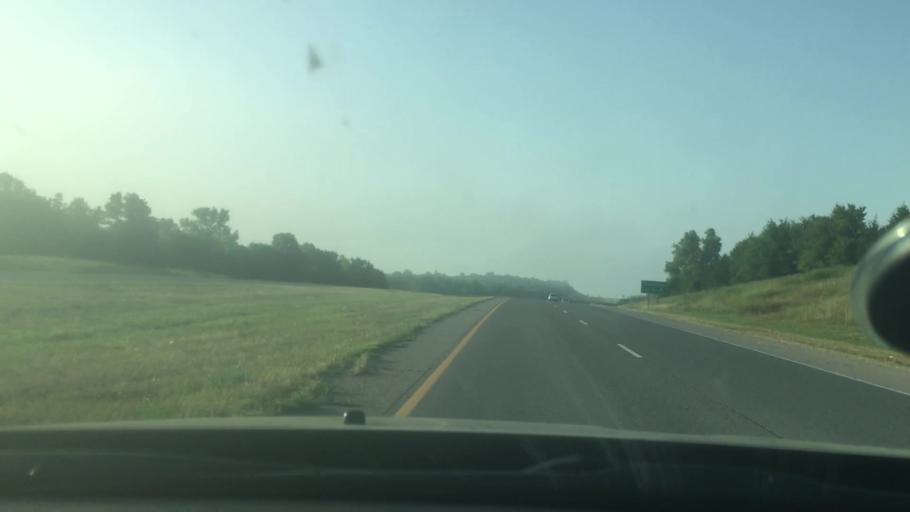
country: US
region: Oklahoma
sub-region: Pontotoc County
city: Ada
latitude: 34.7427
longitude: -96.6487
